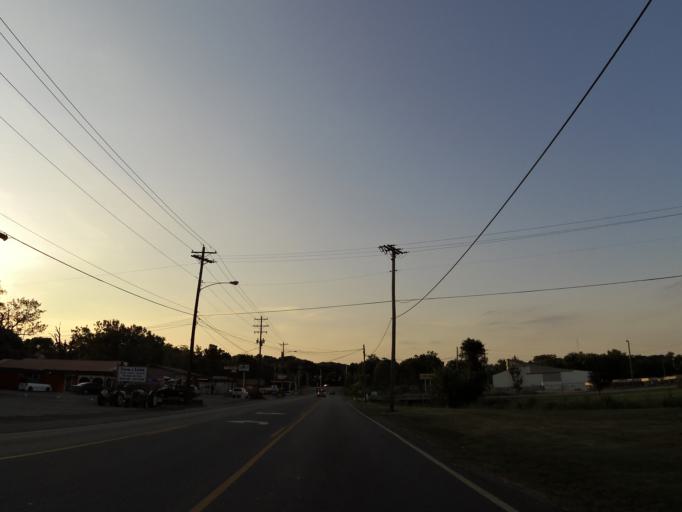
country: US
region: Tennessee
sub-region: Monroe County
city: Sweetwater
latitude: 35.6060
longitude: -84.4609
